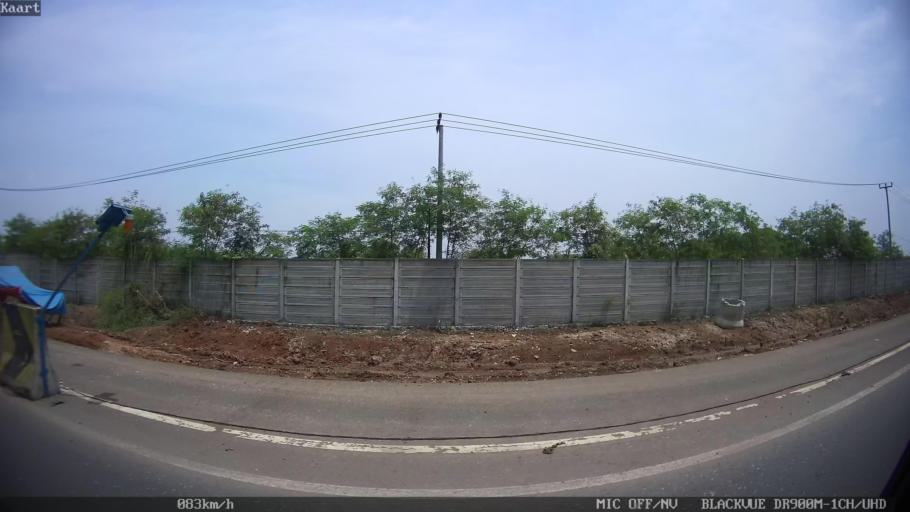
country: ID
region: Banten
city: Serang
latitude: -6.1390
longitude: 106.2584
